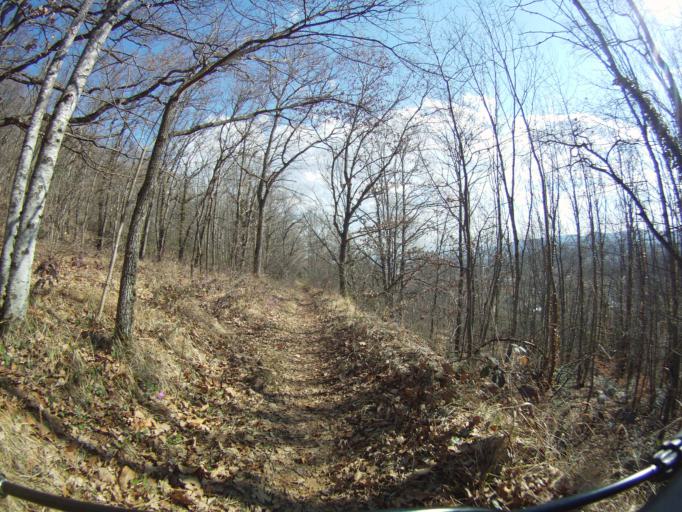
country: FR
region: Auvergne
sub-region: Departement du Puy-de-Dome
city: Royat
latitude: 45.7481
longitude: 3.0513
